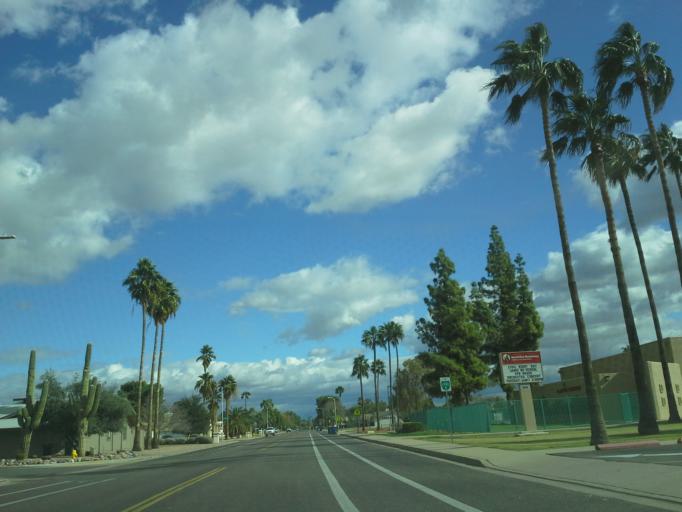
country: US
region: Arizona
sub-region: Maricopa County
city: Mesa
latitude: 33.4442
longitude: -111.8003
